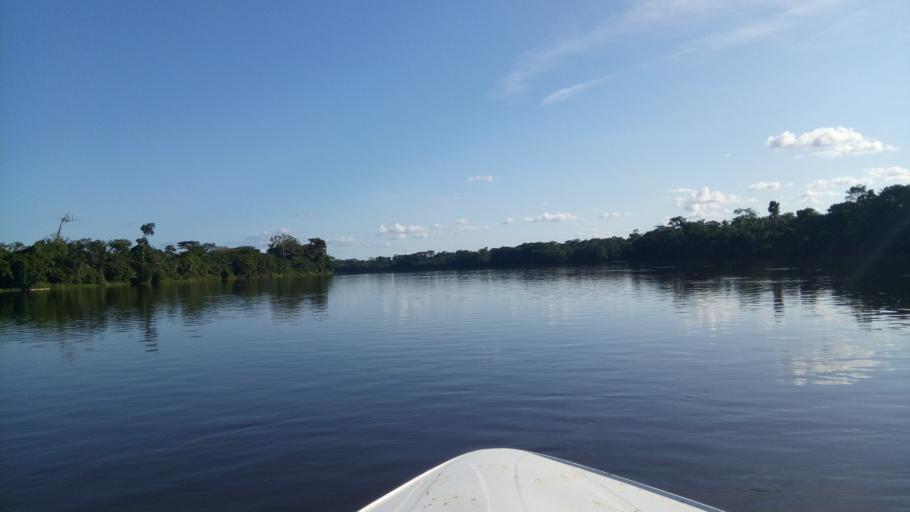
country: CD
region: Eastern Province
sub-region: Sous-Region de la Tshopo
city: Yangambi
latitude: 0.3425
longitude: 24.1327
